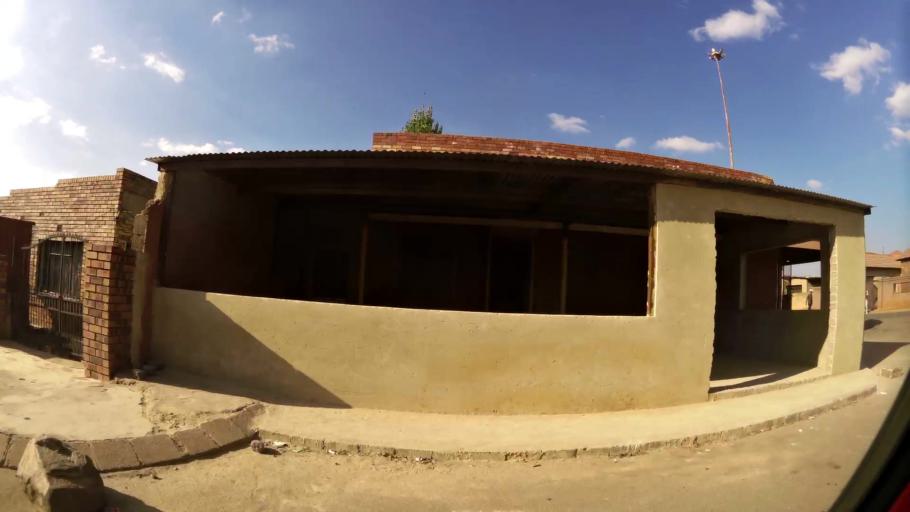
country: ZA
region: Gauteng
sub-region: City of Johannesburg Metropolitan Municipality
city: Soweto
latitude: -26.2273
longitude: 27.8745
